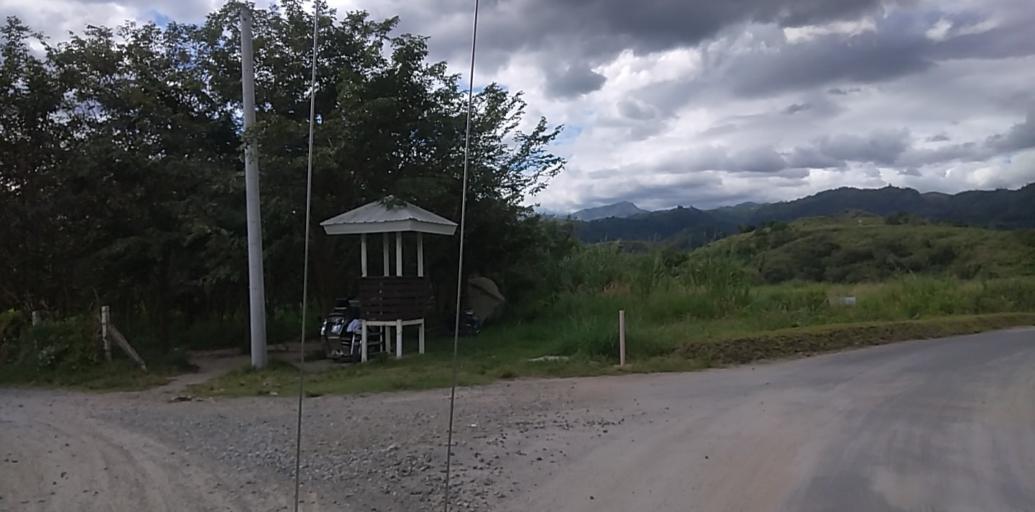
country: PH
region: Central Luzon
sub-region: Province of Pampanga
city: Dolores
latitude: 15.1156
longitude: 120.5052
